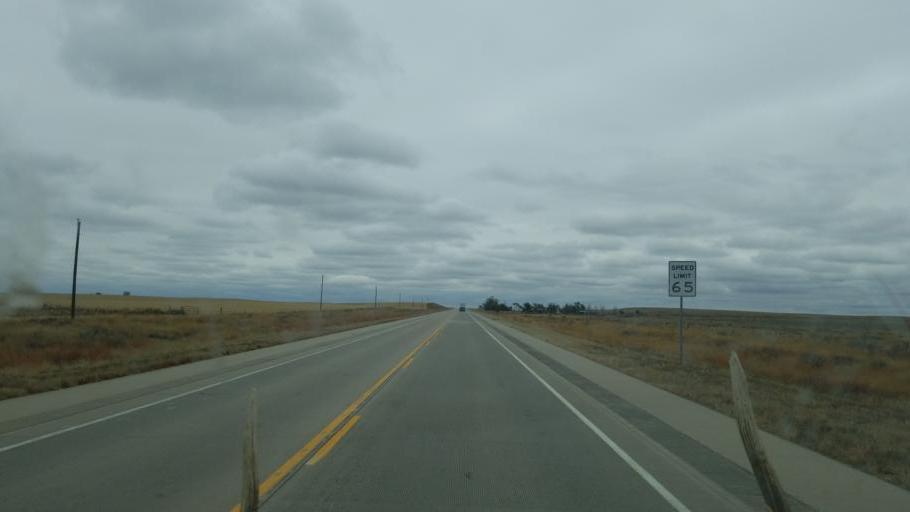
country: US
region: Colorado
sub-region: Kiowa County
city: Eads
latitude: 38.7225
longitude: -102.7761
